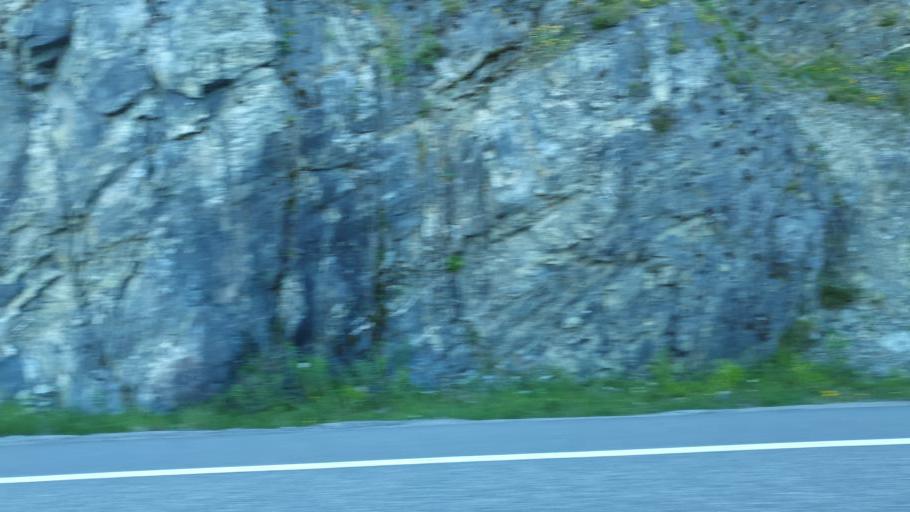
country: NO
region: Sor-Trondelag
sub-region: Rissa
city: Rissa
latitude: 63.5049
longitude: 10.1304
